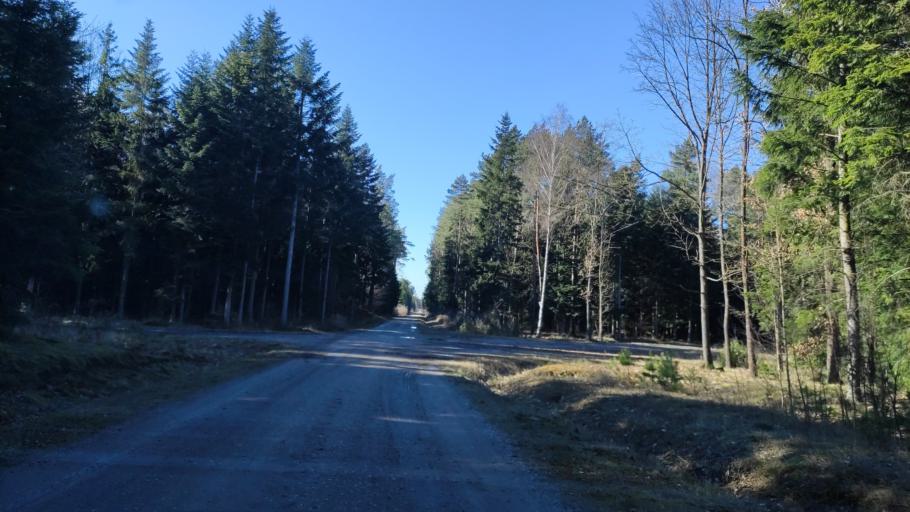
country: PL
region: Masovian Voivodeship
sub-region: Powiat radomski
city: Jedlnia-Letnisko
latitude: 51.4664
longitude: 21.3144
